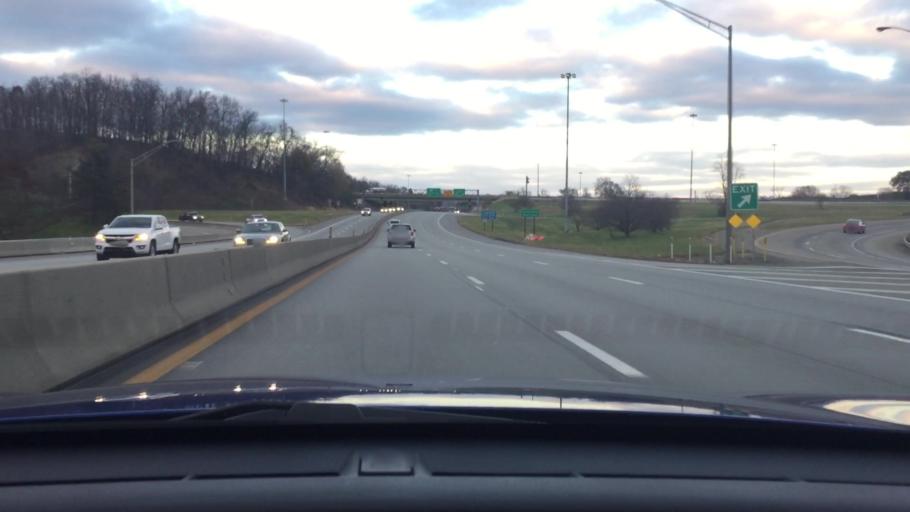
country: US
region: Pennsylvania
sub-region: Westmoreland County
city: New Stanton
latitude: 40.2233
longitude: -79.5972
